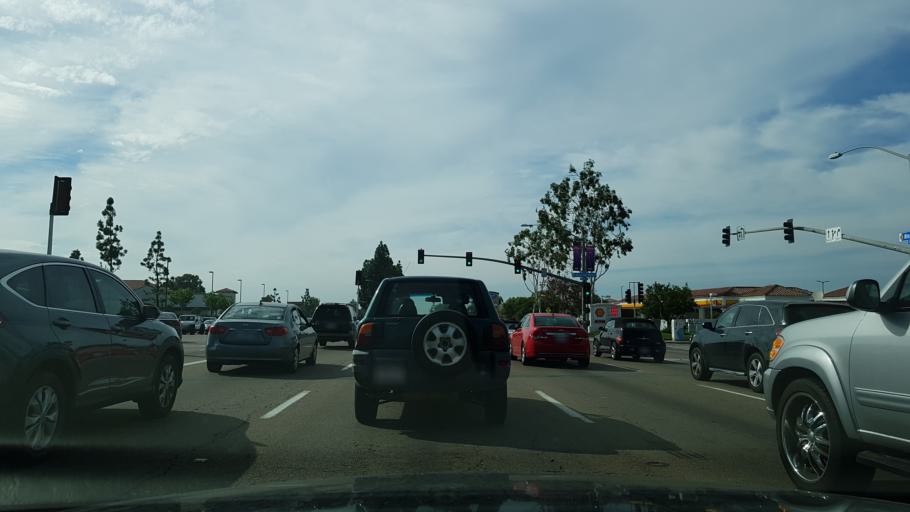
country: US
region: California
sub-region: San Diego County
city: Poway
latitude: 32.9173
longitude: -117.1201
